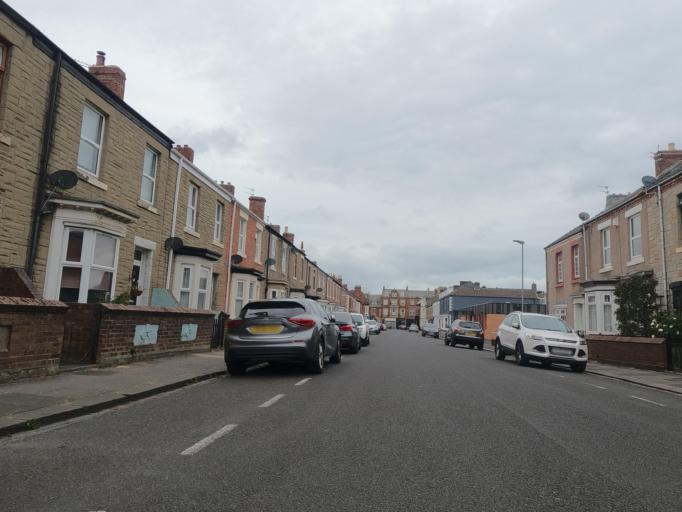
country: GB
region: England
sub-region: Northumberland
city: Blyth
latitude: 55.1260
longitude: -1.5052
